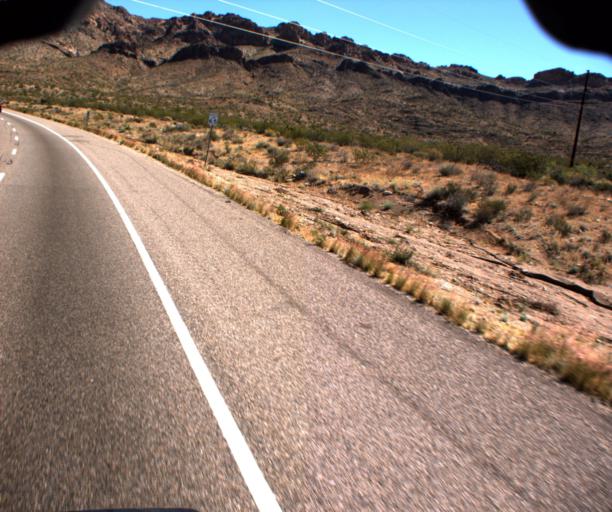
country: US
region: Arizona
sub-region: Mohave County
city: Bullhead City
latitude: 35.1954
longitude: -114.4057
